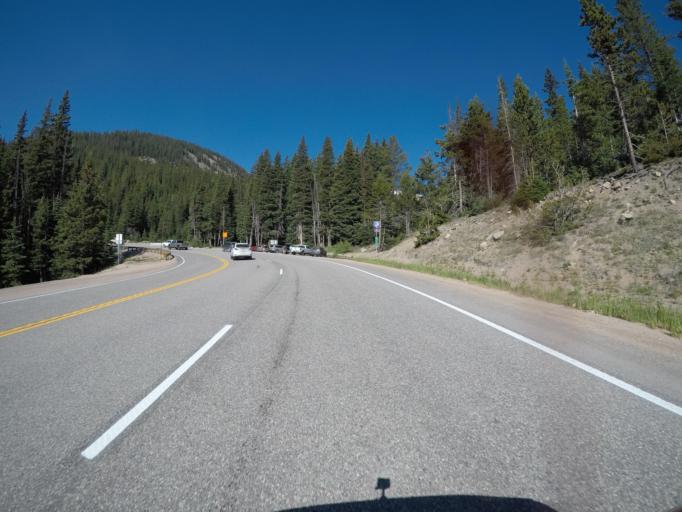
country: US
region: Colorado
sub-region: Grand County
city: Fraser
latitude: 39.8229
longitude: -105.7689
